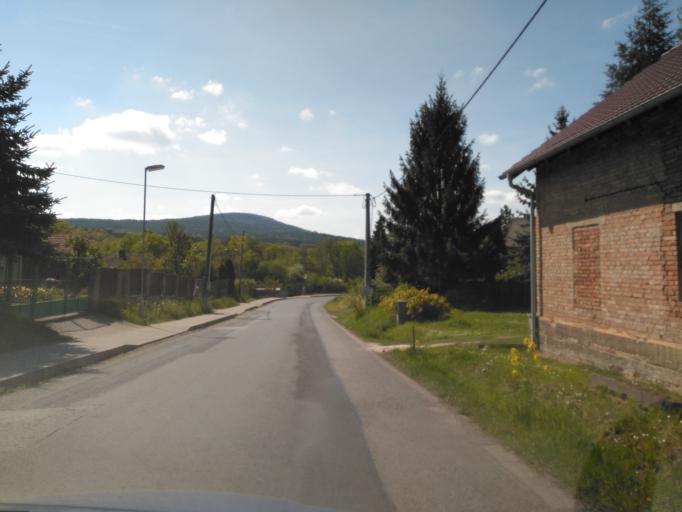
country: CZ
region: Central Bohemia
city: Lochovice
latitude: 49.8451
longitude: 13.9753
